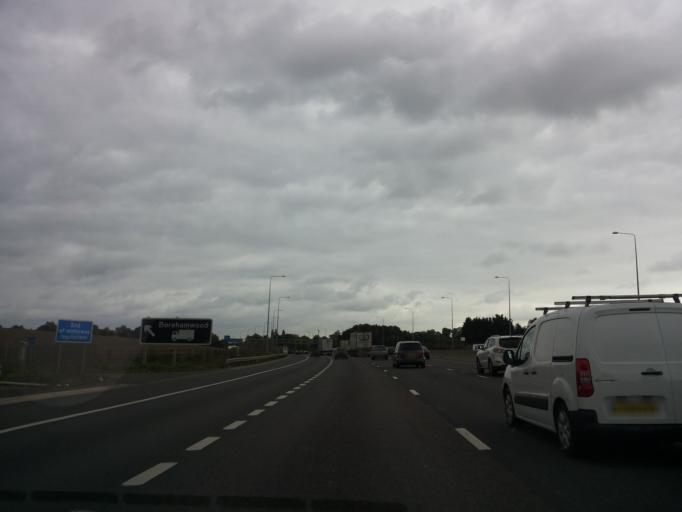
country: GB
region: England
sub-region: Hertfordshire
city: Shenley AV
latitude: 51.6965
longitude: -0.2405
